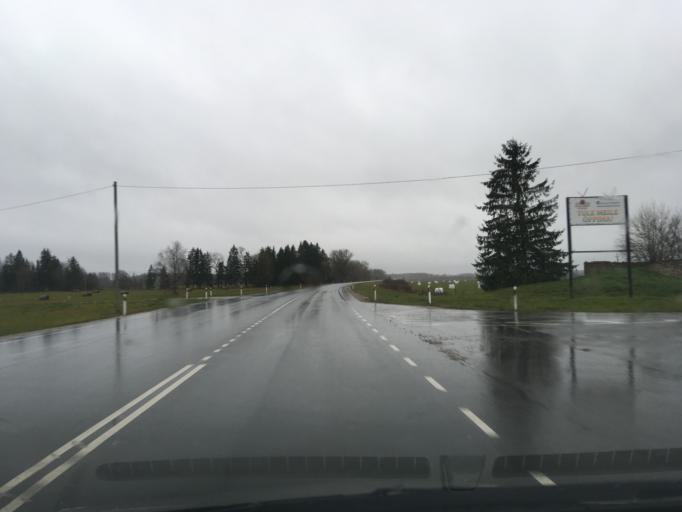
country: EE
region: Harju
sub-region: Nissi vald
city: Turba
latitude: 58.8747
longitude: 24.0858
